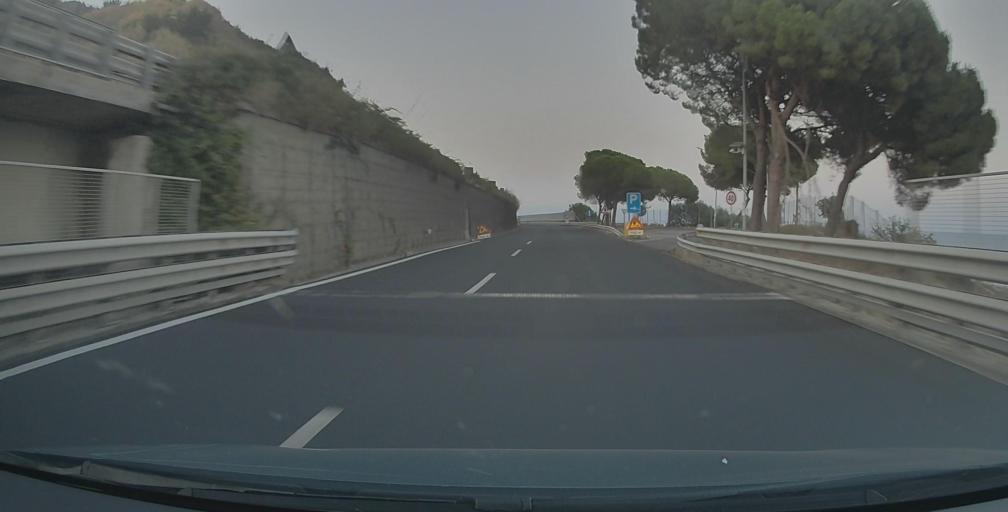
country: IT
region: Sicily
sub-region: Messina
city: Letojanni
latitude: 37.8821
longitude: 15.3061
